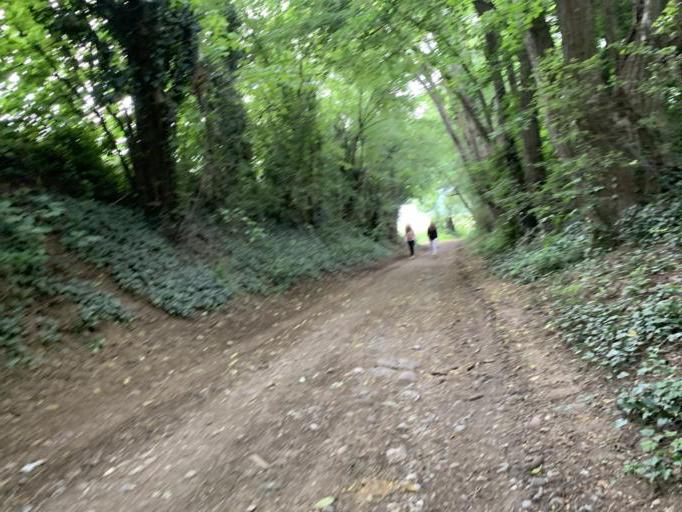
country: FR
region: Alsace
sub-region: Departement du Haut-Rhin
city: Morschwiller-le-Bas
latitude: 47.7313
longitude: 7.2699
